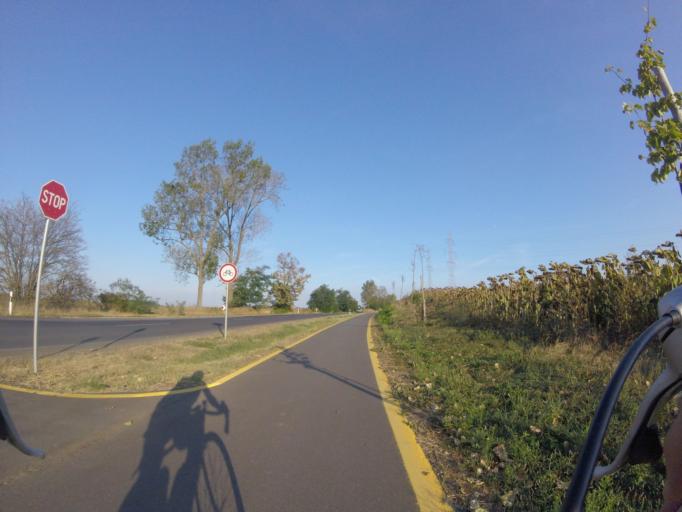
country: HU
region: Szabolcs-Szatmar-Bereg
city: Tiszanagyfalu
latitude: 48.0624
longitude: 21.5462
